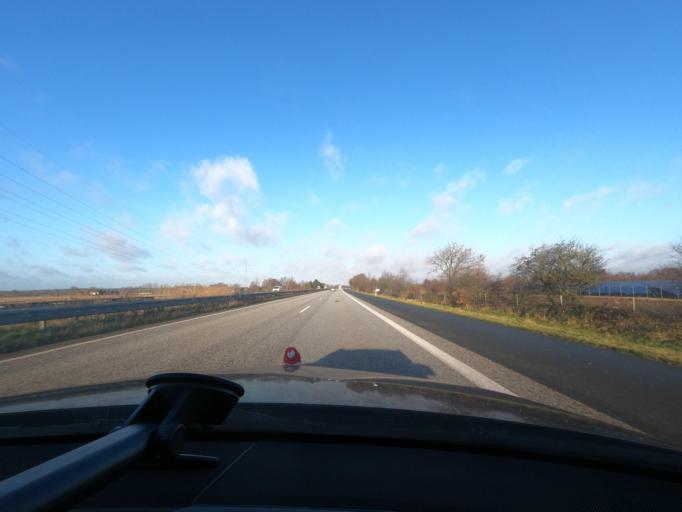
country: DE
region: Schleswig-Holstein
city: Lurschau
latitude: 54.5575
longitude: 9.4678
